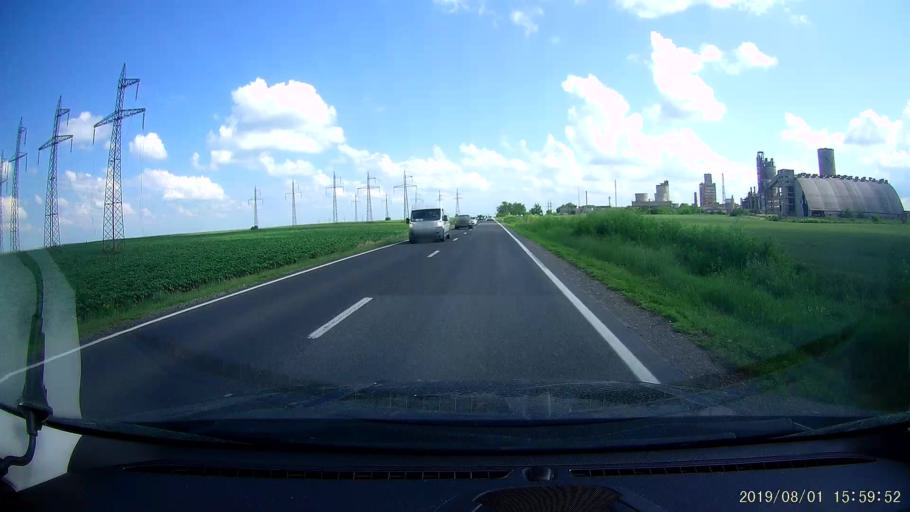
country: RO
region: Ialomita
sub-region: Comuna Slobozia
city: Slobozia
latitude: 44.5395
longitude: 27.3865
